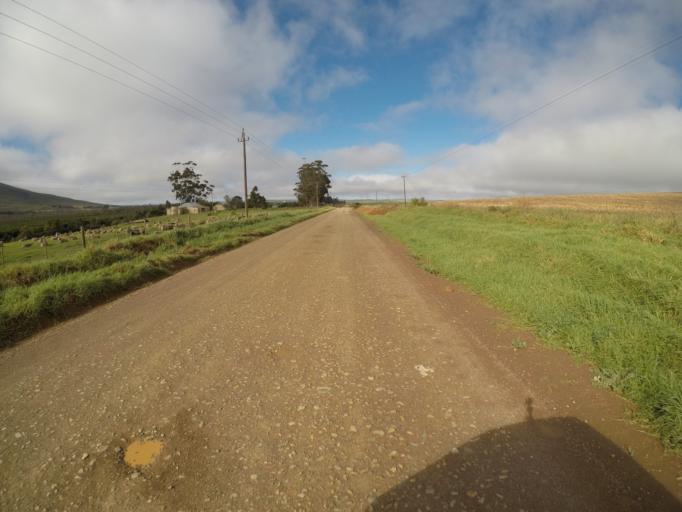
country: ZA
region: Western Cape
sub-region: Cape Winelands District Municipality
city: Ashton
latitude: -34.1325
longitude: 19.8554
